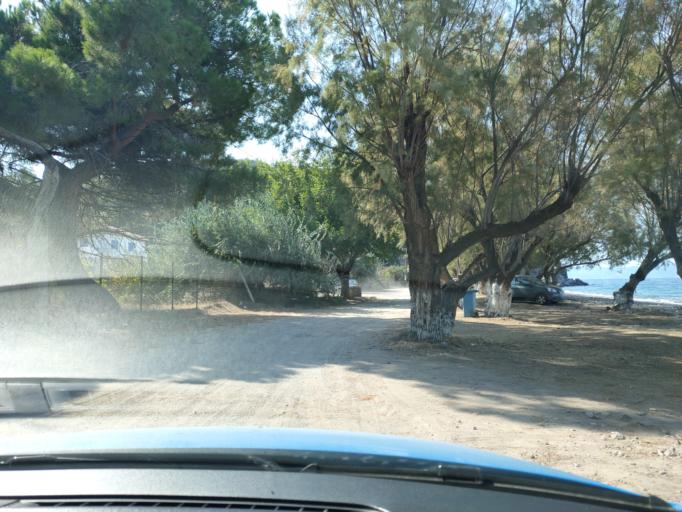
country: GR
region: North Aegean
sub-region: Nomos Lesvou
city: Mantamados
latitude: 39.3744
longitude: 26.3106
